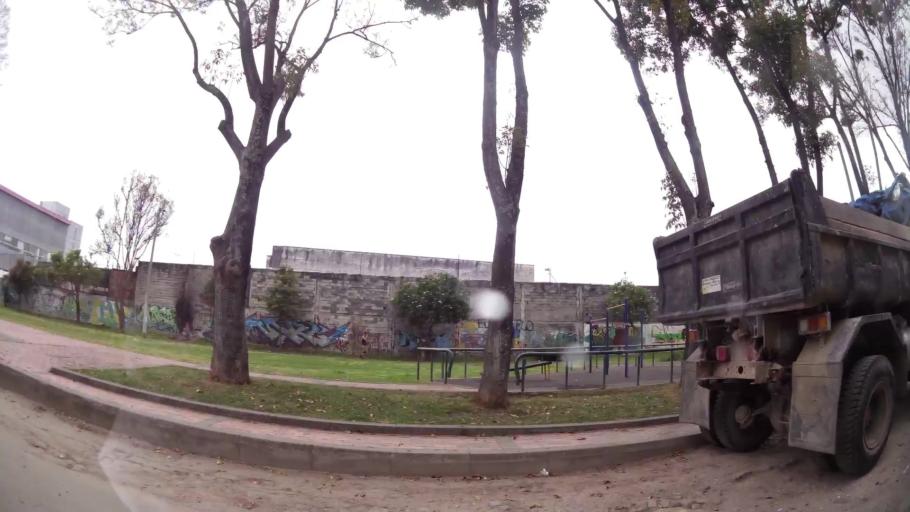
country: CO
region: Bogota D.C.
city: Barrio San Luis
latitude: 4.6770
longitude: -74.0879
